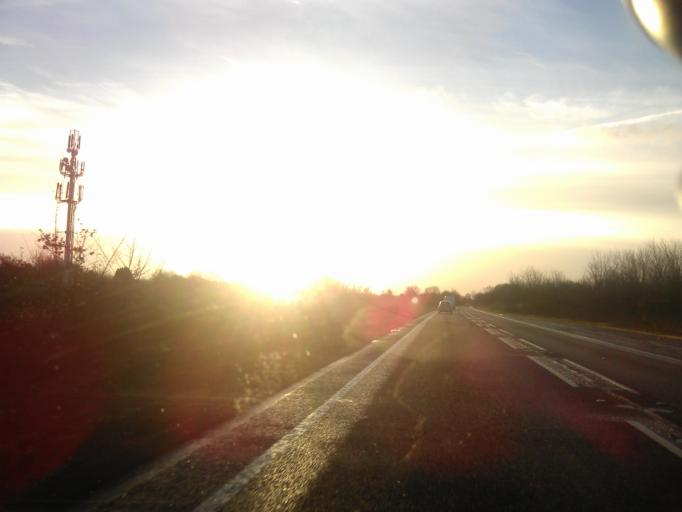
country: GB
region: England
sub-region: Essex
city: Little Clacton
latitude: 51.8331
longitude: 1.1275
